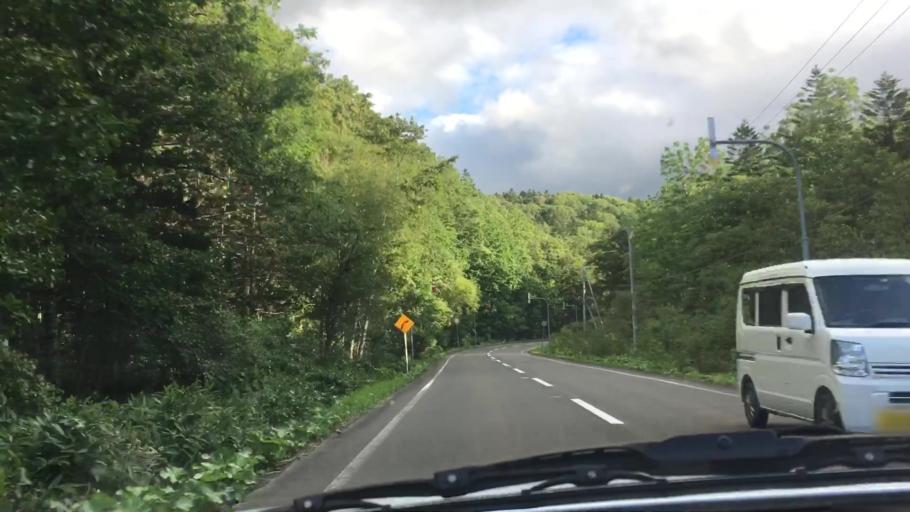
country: JP
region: Hokkaido
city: Shimo-furano
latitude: 43.0979
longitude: 142.6855
